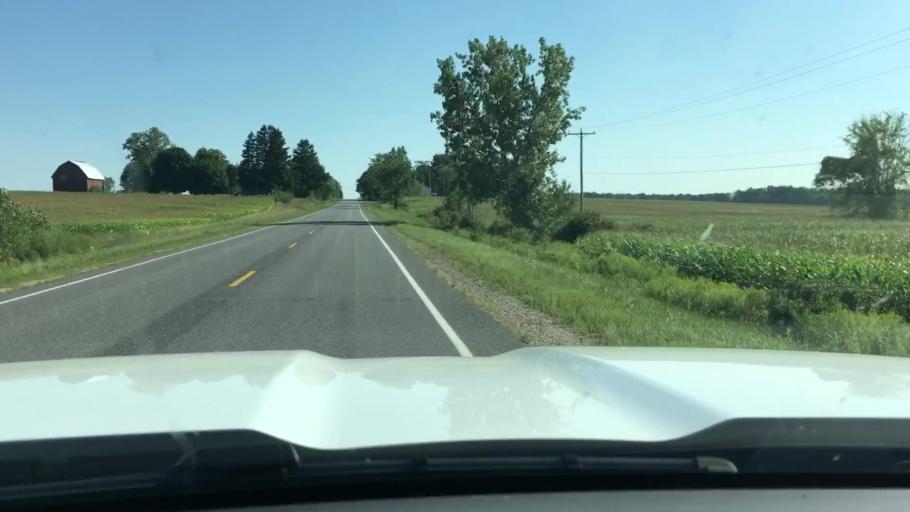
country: US
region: Michigan
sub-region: Muskegon County
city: Ravenna
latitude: 43.1688
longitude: -85.9280
